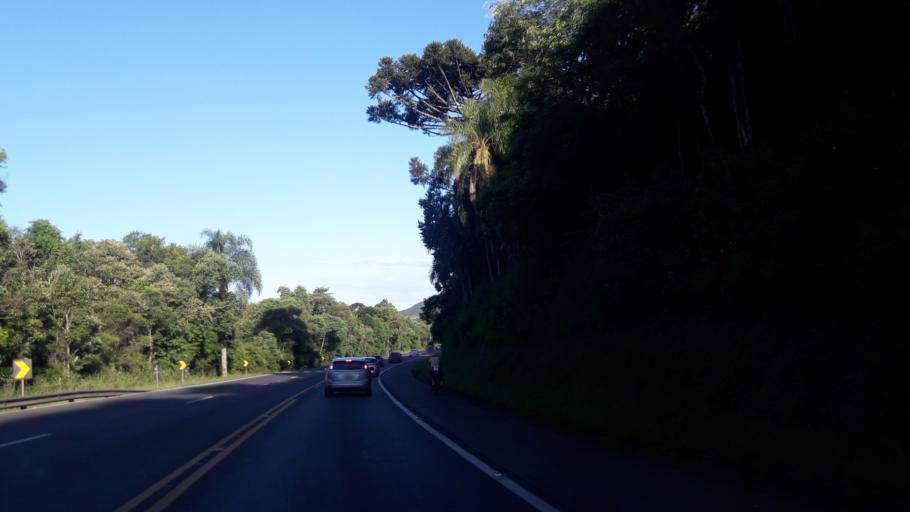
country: BR
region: Parana
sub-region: Prudentopolis
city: Prudentopolis
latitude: -25.3122
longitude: -51.1839
